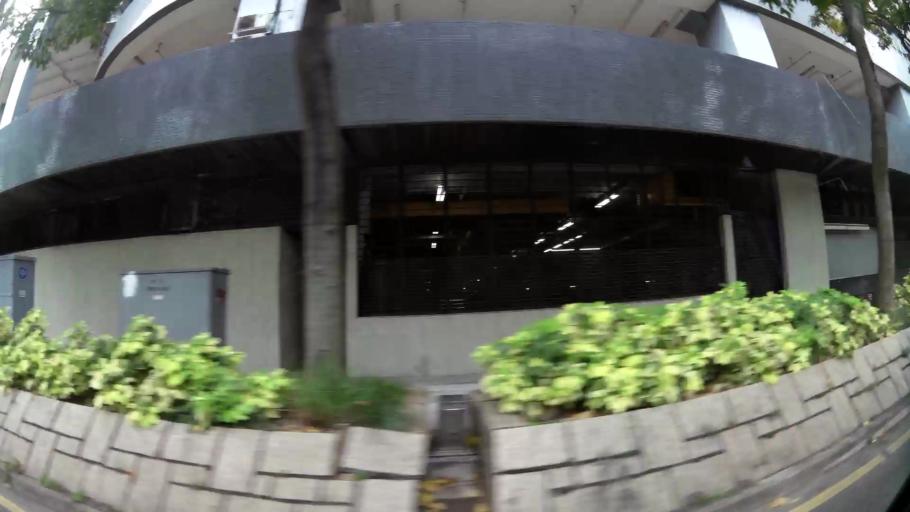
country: HK
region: Kowloon City
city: Kowloon
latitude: 22.3256
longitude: 114.2083
